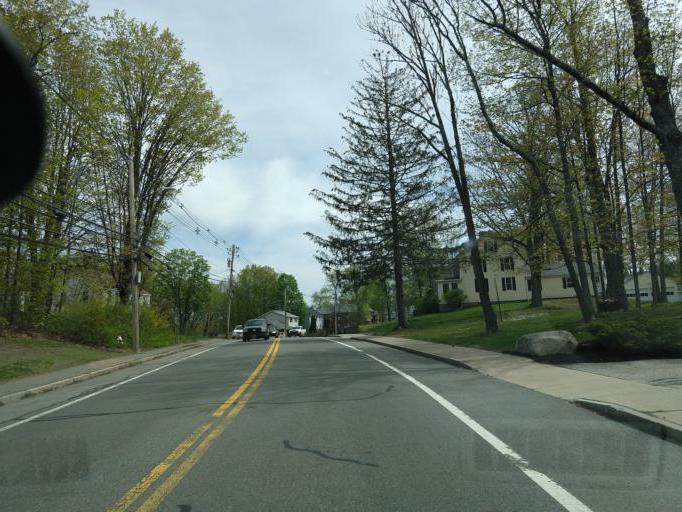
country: US
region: Massachusetts
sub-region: Essex County
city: Merrimac
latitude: 42.8347
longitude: -70.9976
